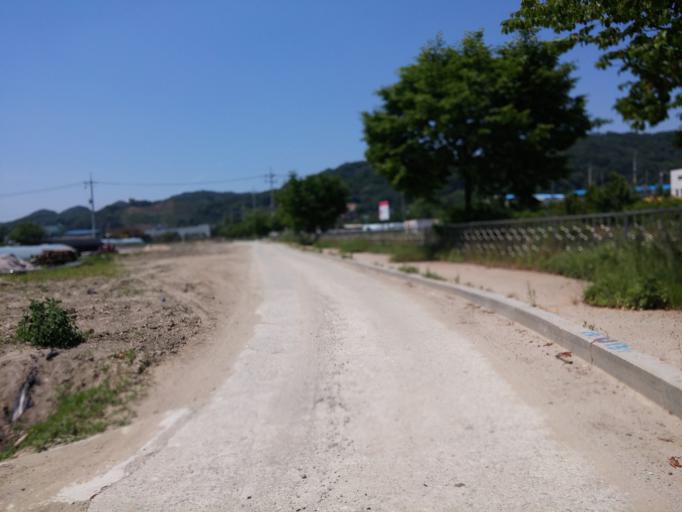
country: KR
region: Chungcheongbuk-do
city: Cheongju-si
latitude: 36.5591
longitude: 127.4349
